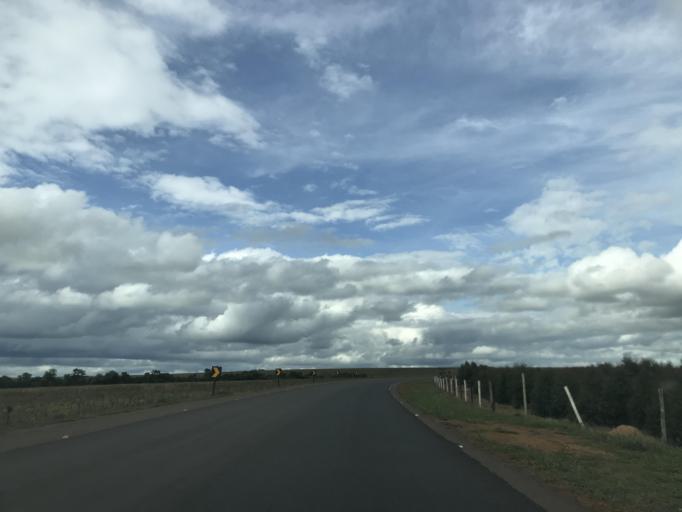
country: BR
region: Goias
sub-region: Vianopolis
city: Vianopolis
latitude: -16.9802
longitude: -48.6673
